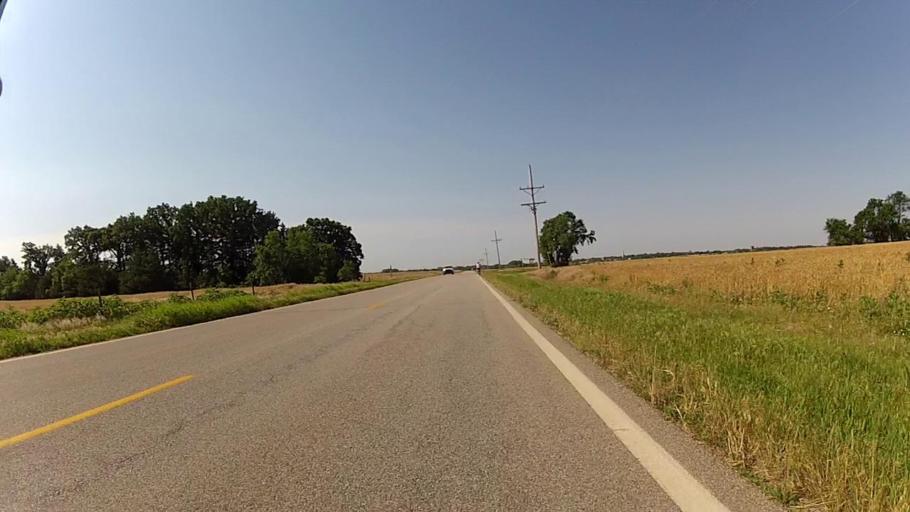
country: US
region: Kansas
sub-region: Sumner County
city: Caldwell
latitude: 37.0558
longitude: -97.6008
